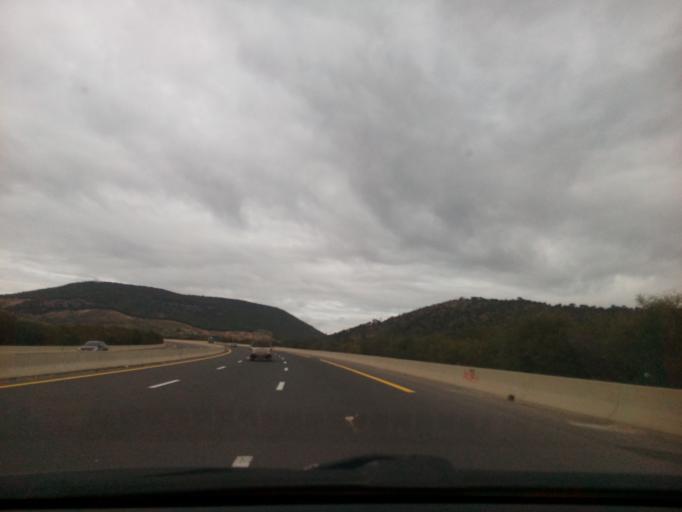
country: DZ
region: Sidi Bel Abbes
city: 'Ain el Berd
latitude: 35.3692
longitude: -0.5000
